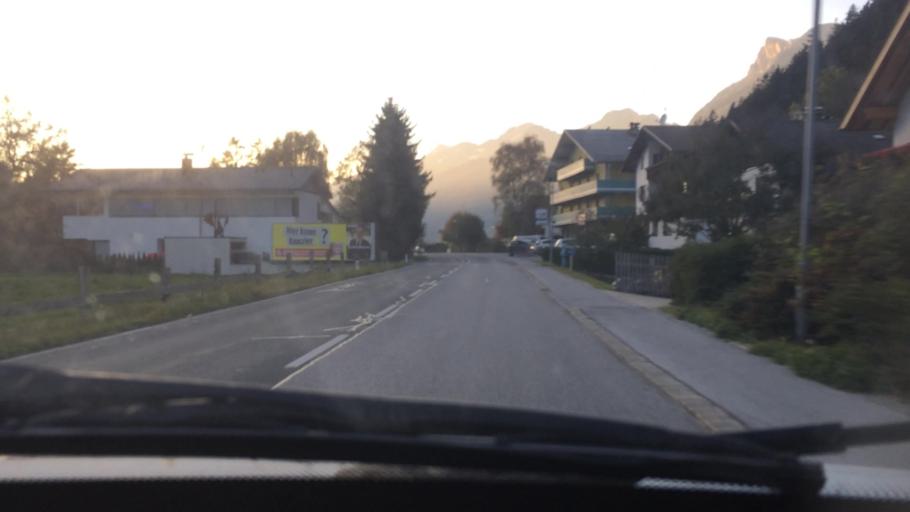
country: AT
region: Tyrol
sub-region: Politischer Bezirk Innsbruck Land
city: Polling in Tirol
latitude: 47.2930
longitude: 11.1578
